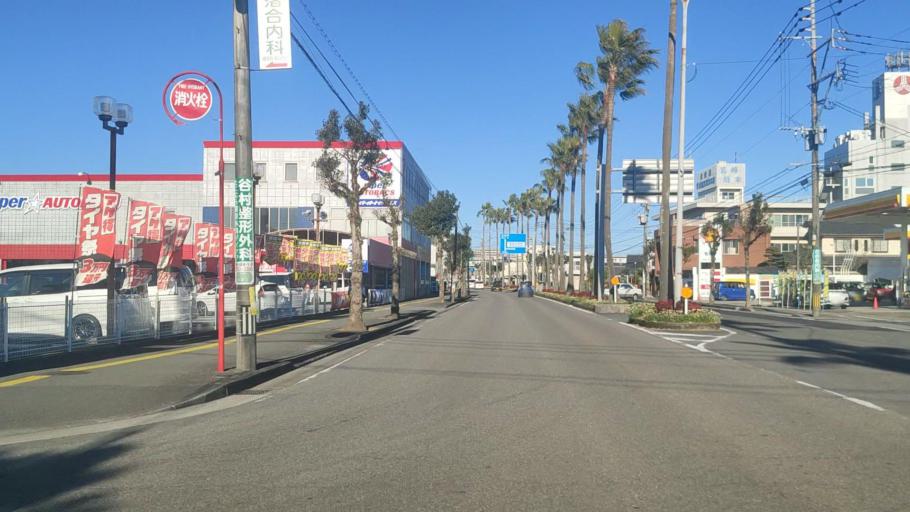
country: JP
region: Miyazaki
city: Miyazaki-shi
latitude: 31.8969
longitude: 131.4231
